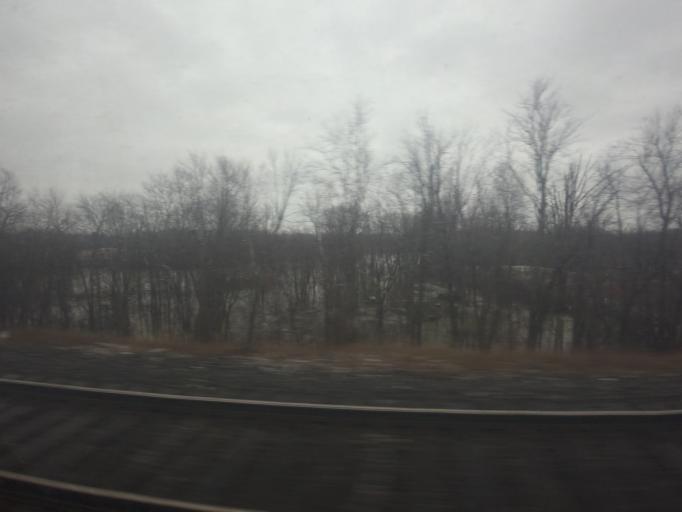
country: CA
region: Ontario
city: Gananoque
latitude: 44.3591
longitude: -76.1943
